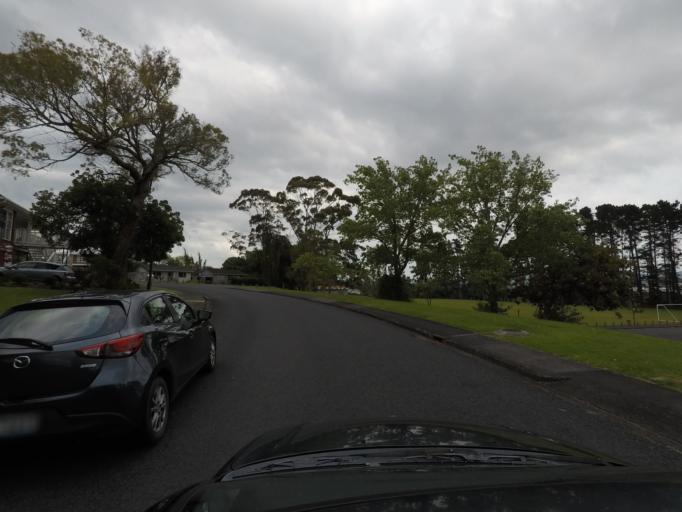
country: NZ
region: Auckland
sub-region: Auckland
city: Rosebank
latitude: -36.8471
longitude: 174.6452
